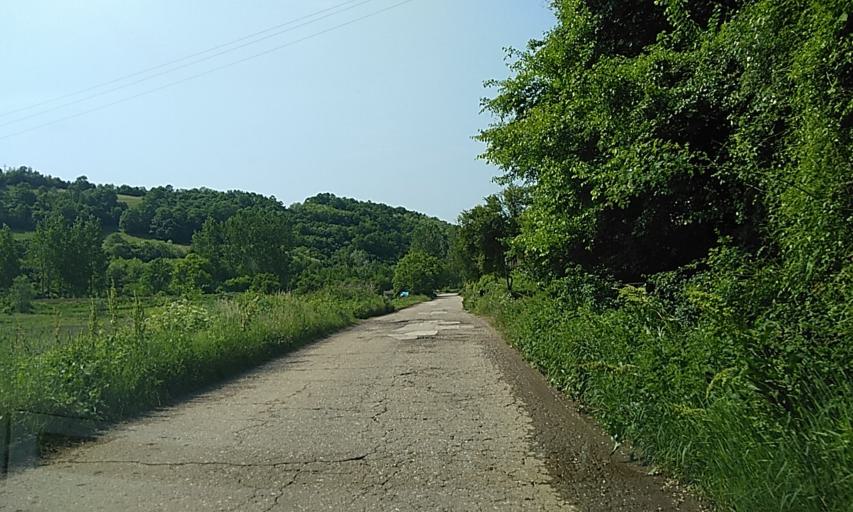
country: RS
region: Central Serbia
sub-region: Pcinjski Okrug
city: Vladicin Han
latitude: 42.7303
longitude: 22.0634
